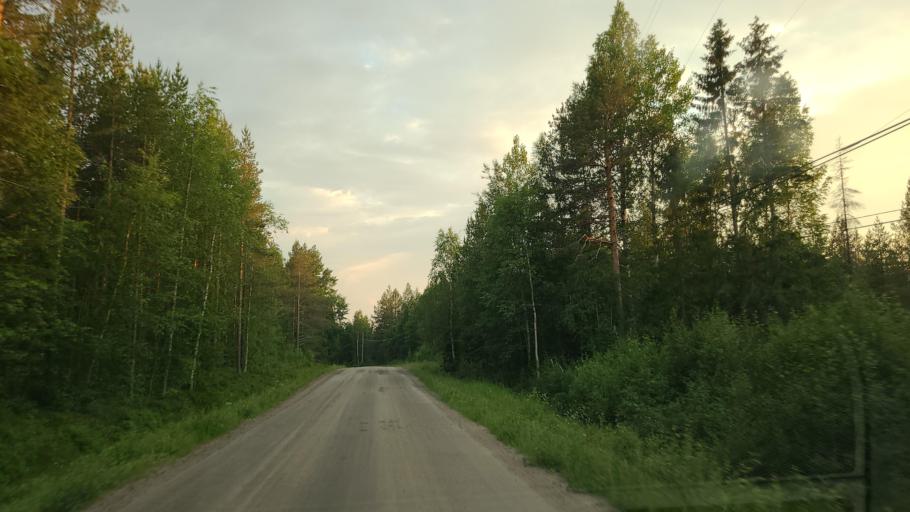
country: SE
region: Vaesterbotten
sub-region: Robertsfors Kommun
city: Robertsfors
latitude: 64.0696
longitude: 20.8755
